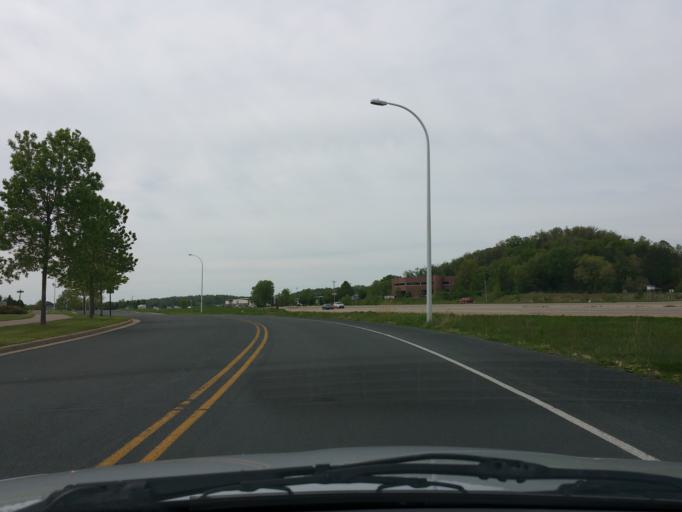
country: US
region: Wisconsin
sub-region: Pierce County
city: River Falls
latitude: 44.8871
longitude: -92.6296
